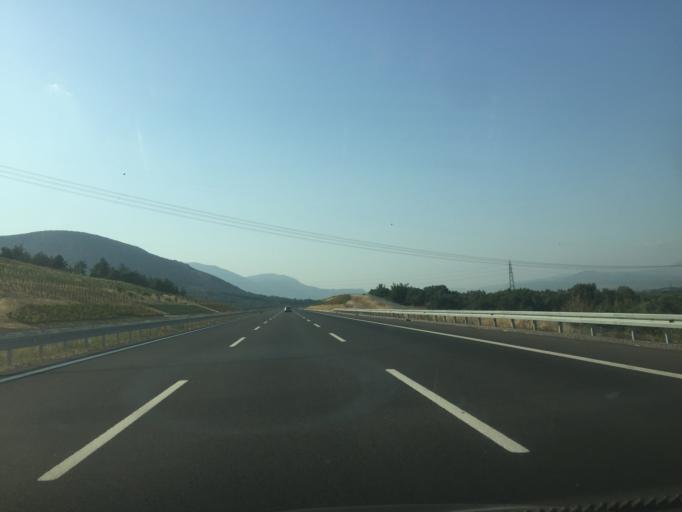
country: TR
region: Manisa
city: Kirkagac
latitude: 39.0585
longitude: 27.7257
